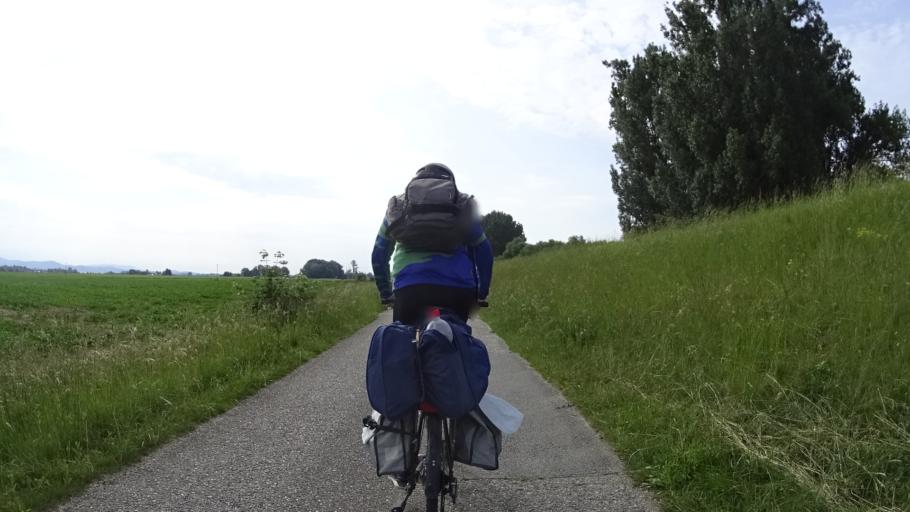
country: DE
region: Bavaria
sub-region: Lower Bavaria
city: Irlbach
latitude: 48.8392
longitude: 12.7730
